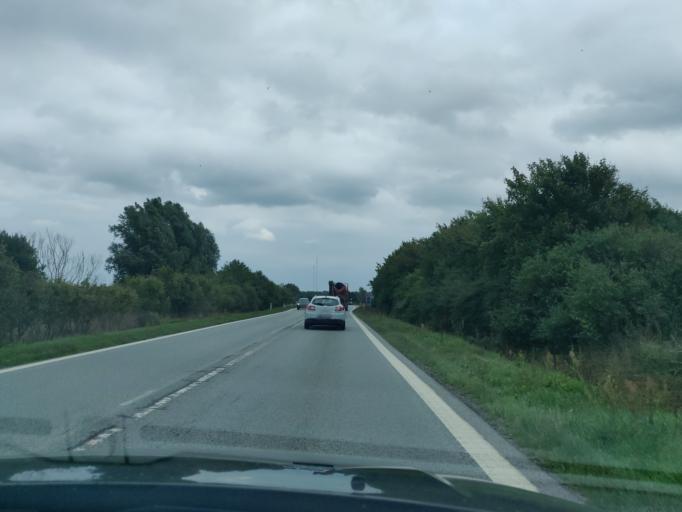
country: DK
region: North Denmark
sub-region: Alborg Kommune
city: Frejlev
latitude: 57.0112
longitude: 9.7705
